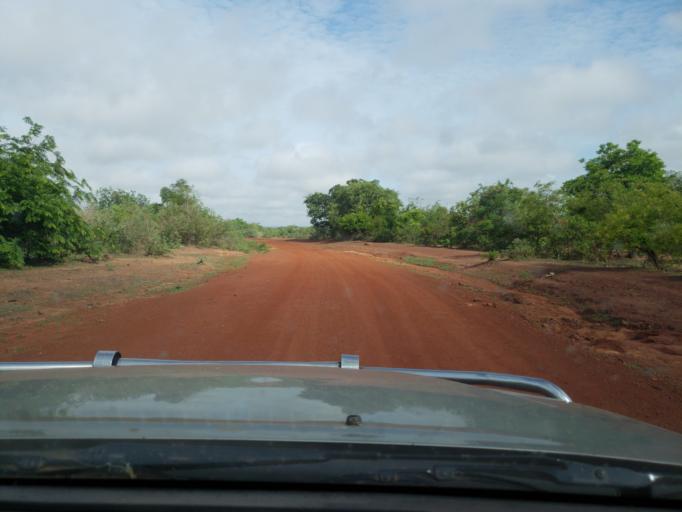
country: ML
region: Sikasso
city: Koutiala
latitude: 12.3930
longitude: -5.9788
